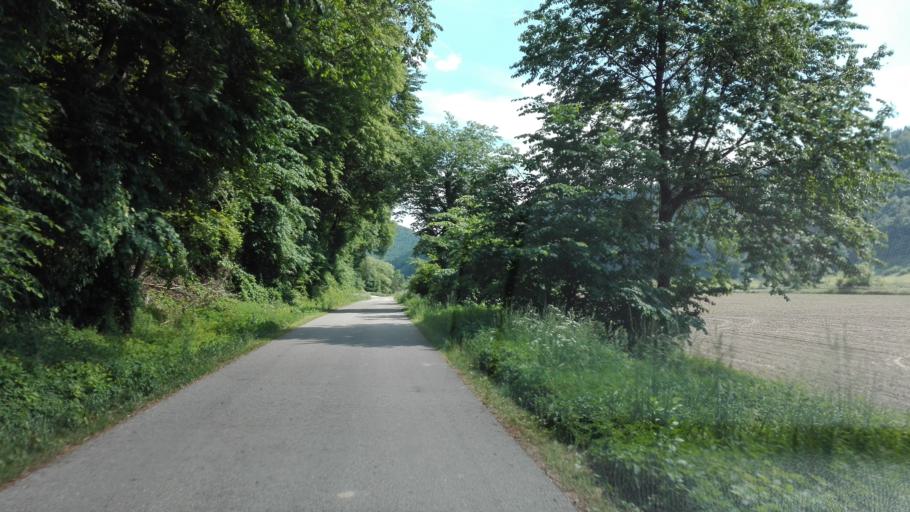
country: AT
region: Upper Austria
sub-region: Politischer Bezirk Rohrbach
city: Pfarrkirchen im Muehlkreis
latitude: 48.4410
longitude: 13.8600
